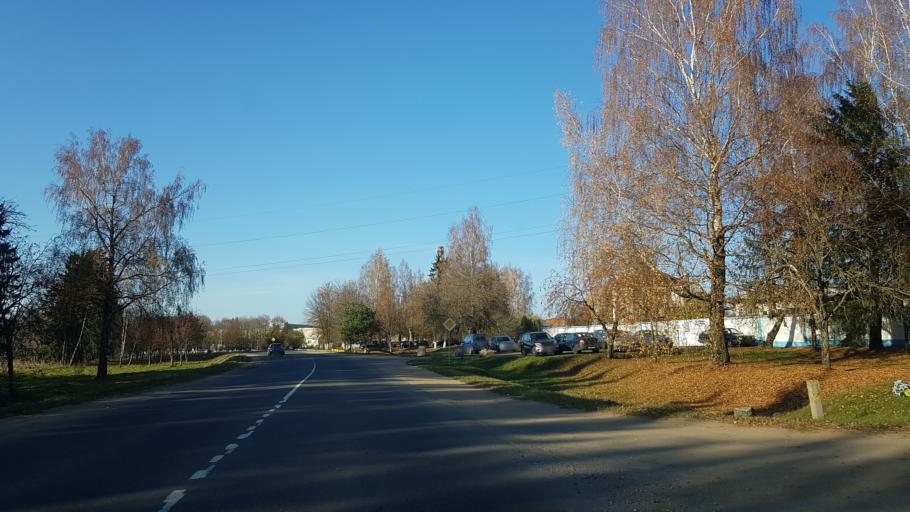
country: BY
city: Fanipol
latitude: 53.7327
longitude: 27.3314
